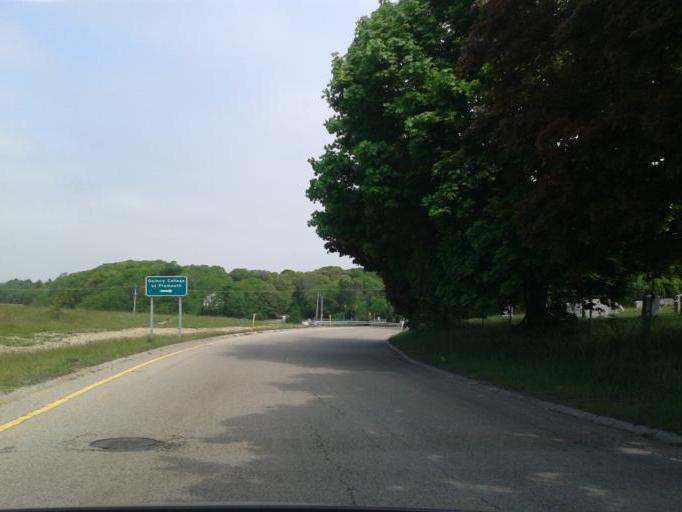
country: US
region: Massachusetts
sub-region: Plymouth County
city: Plymouth
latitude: 41.9532
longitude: -70.6805
